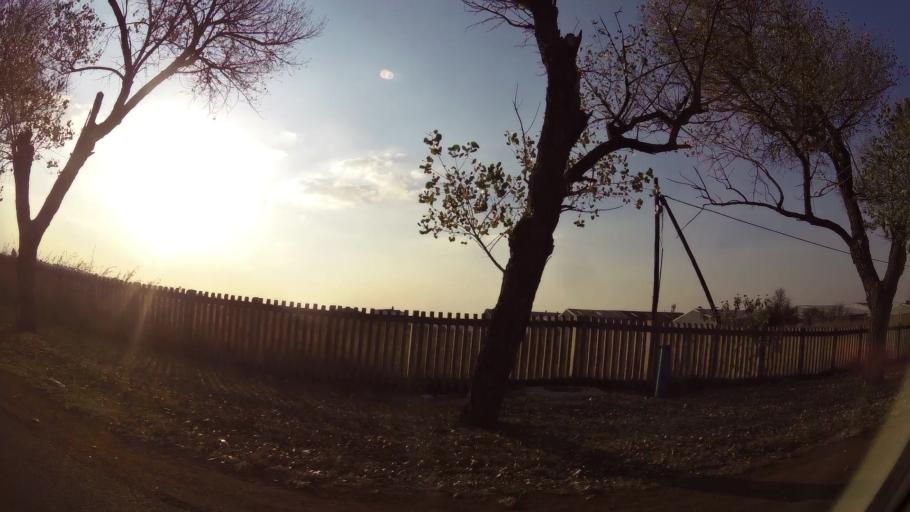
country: ZA
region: Gauteng
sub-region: Ekurhuleni Metropolitan Municipality
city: Springs
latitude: -26.2547
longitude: 28.3987
